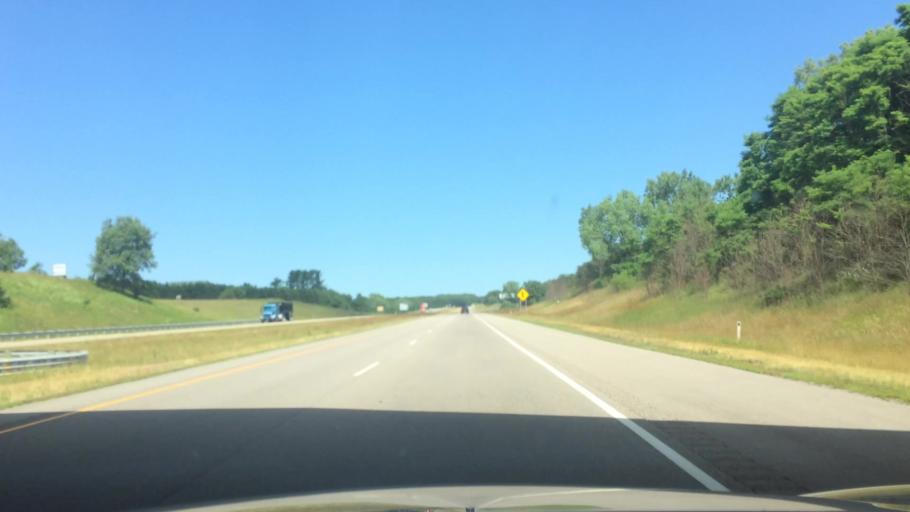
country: US
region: Wisconsin
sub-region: Marquette County
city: Westfield
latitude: 44.0351
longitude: -89.5286
